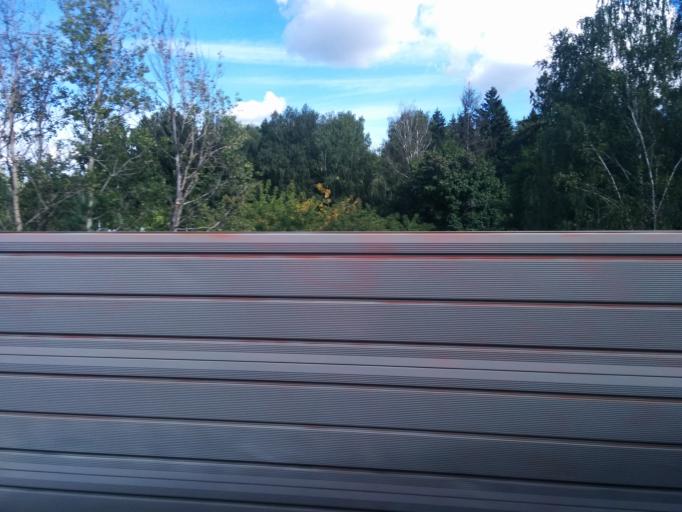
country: RU
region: Moskovskaya
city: Sheremet'yevskiy
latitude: 55.9936
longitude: 37.4946
